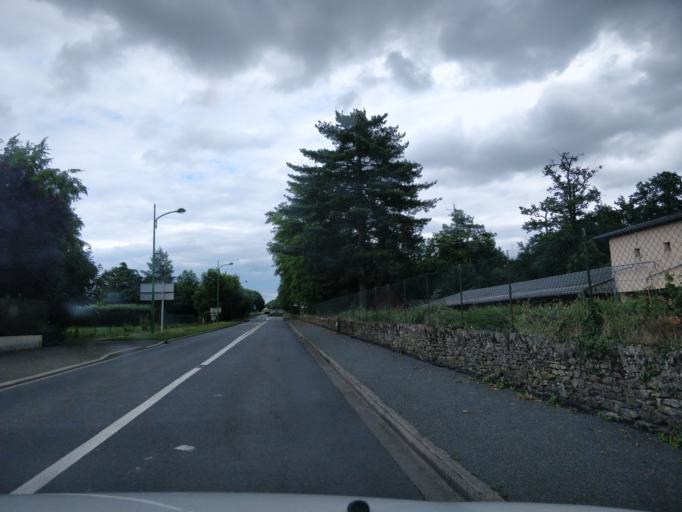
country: FR
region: Pays de la Loire
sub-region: Departement de Maine-et-Loire
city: Grez-Neuville
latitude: 47.6310
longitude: -0.7088
